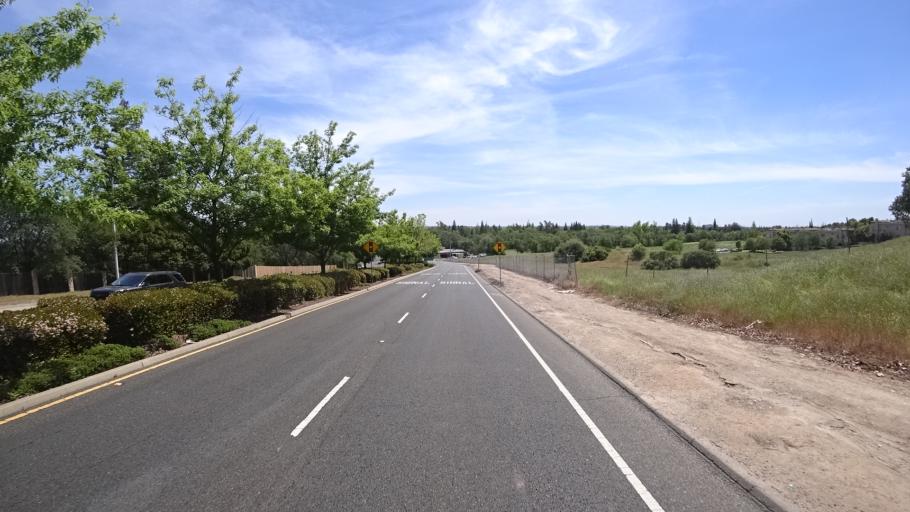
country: US
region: California
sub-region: Placer County
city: Rocklin
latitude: 38.7881
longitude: -121.2551
